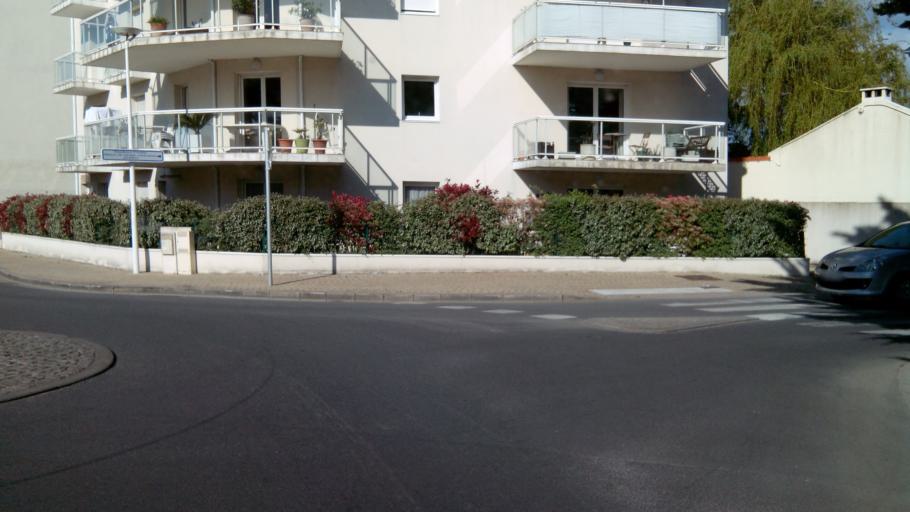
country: FR
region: Pays de la Loire
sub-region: Departement de la Loire-Atlantique
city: Pornichet
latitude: 47.2596
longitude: -2.3351
